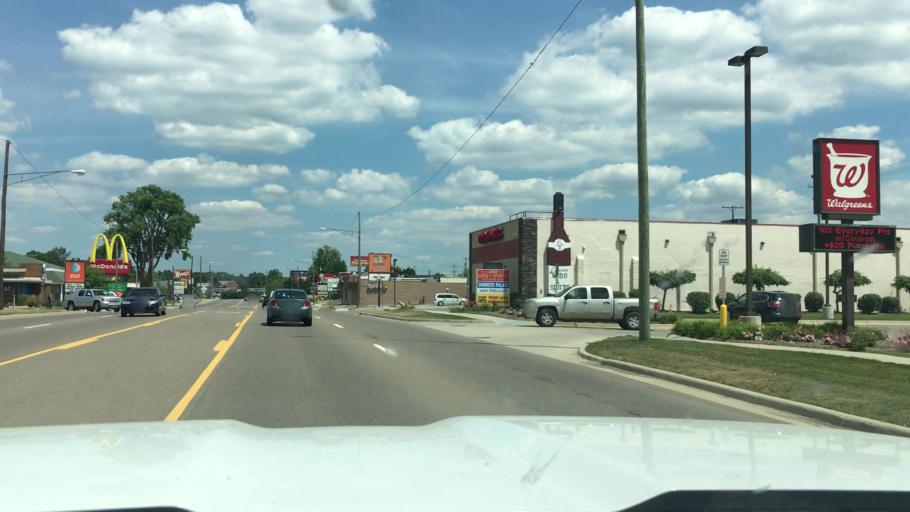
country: US
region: Michigan
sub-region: Lapeer County
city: Lapeer
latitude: 43.0444
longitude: -83.3197
